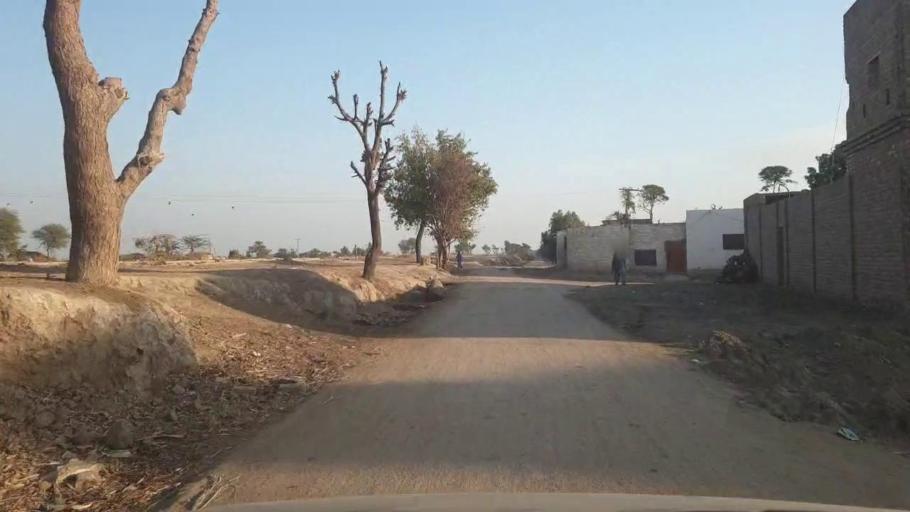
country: PK
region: Sindh
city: Chambar
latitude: 25.2935
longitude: 68.8933
